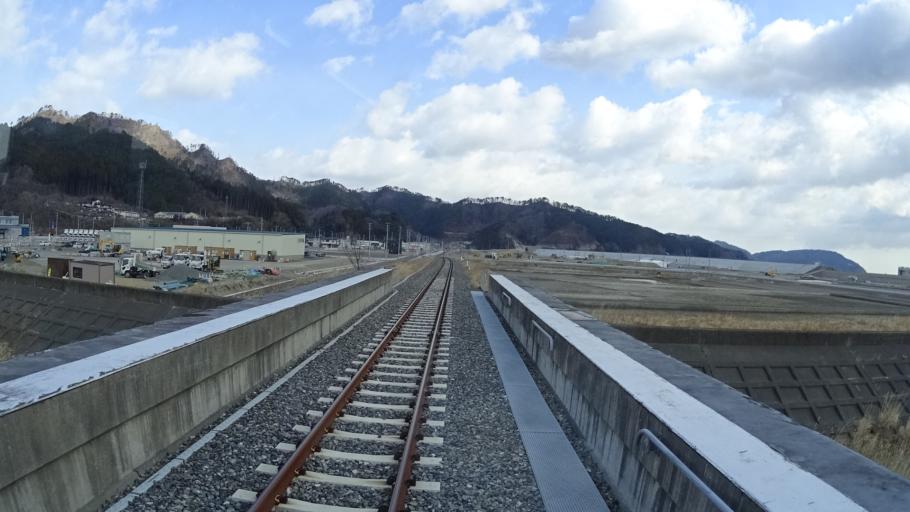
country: JP
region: Iwate
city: Otsuchi
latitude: 39.3302
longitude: 141.8897
